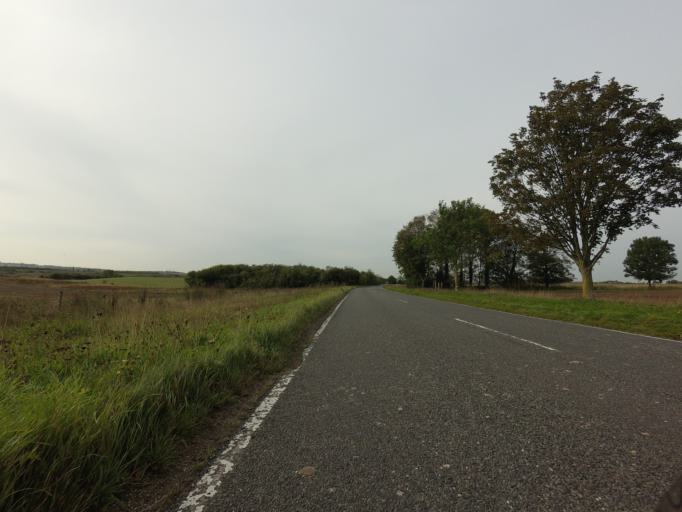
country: GB
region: England
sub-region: Cambridgeshire
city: Melbourn
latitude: 52.0715
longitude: 0.0600
